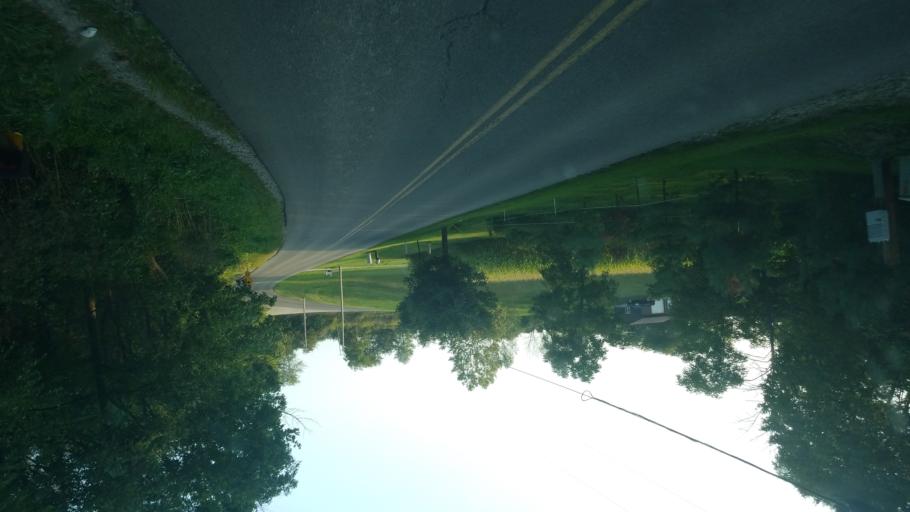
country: US
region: Ohio
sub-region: Wayne County
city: Shreve
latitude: 40.6662
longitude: -81.9708
